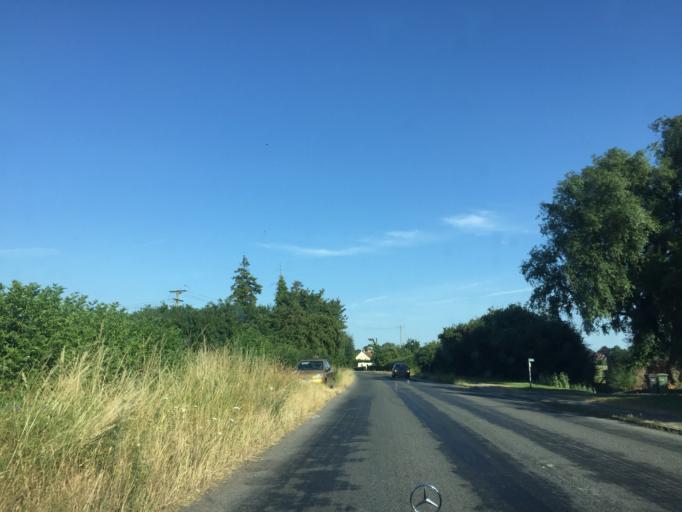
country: GB
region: England
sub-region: Oxfordshire
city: Thame
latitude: 51.7143
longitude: -1.0136
